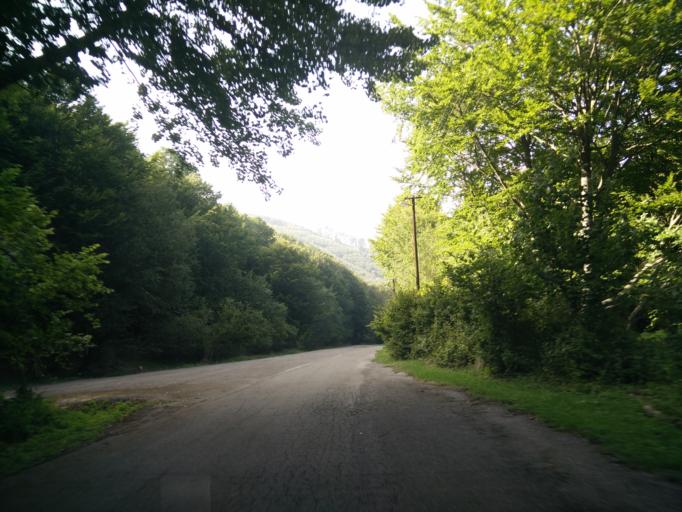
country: SK
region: Nitriansky
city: Novaky
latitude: 48.6615
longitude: 18.6316
